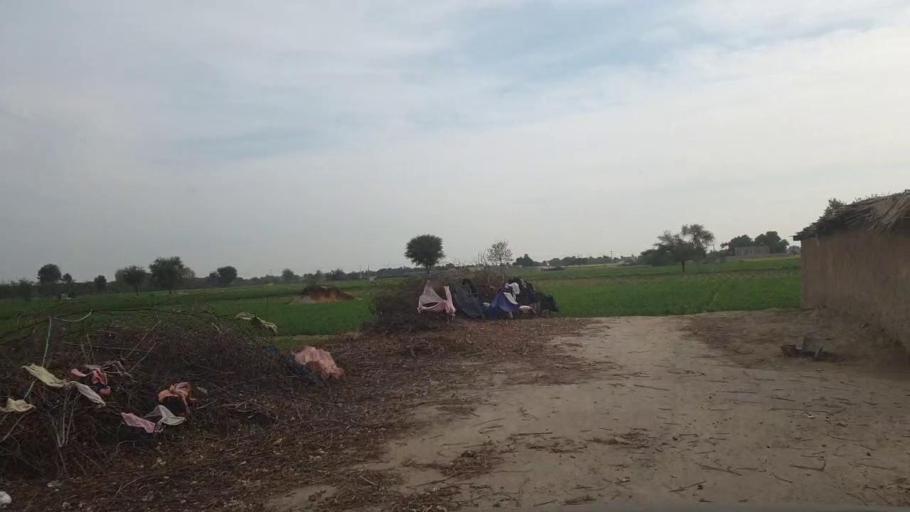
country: PK
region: Sindh
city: Shahpur Chakar
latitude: 26.1149
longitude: 68.5256
